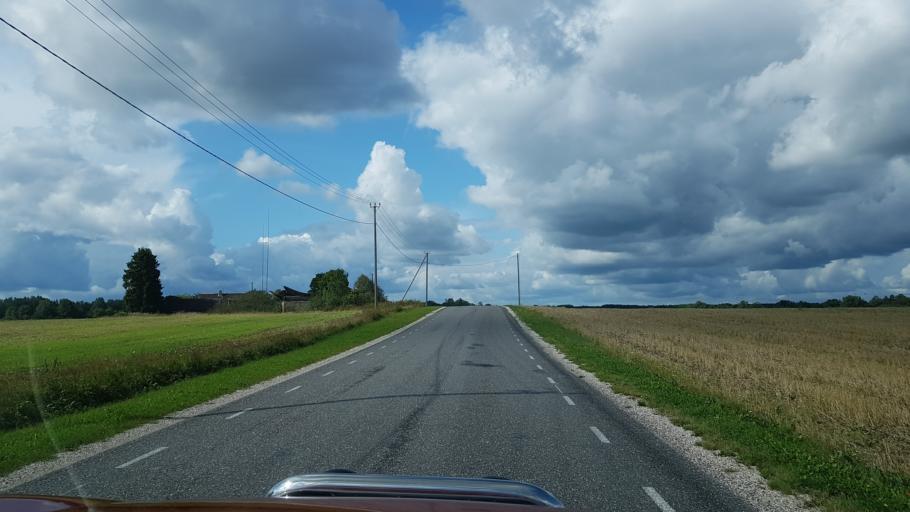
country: EE
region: Harju
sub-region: Keila linn
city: Keila
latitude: 59.1959
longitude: 24.4585
